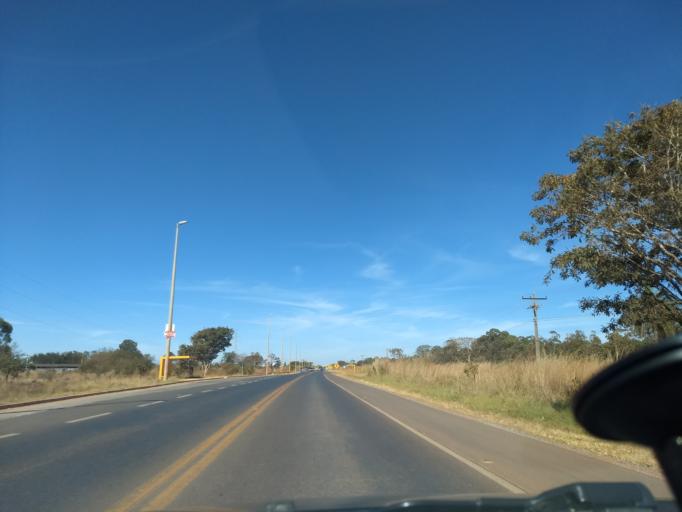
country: BR
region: Federal District
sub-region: Brasilia
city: Brasilia
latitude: -15.7770
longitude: -48.0469
